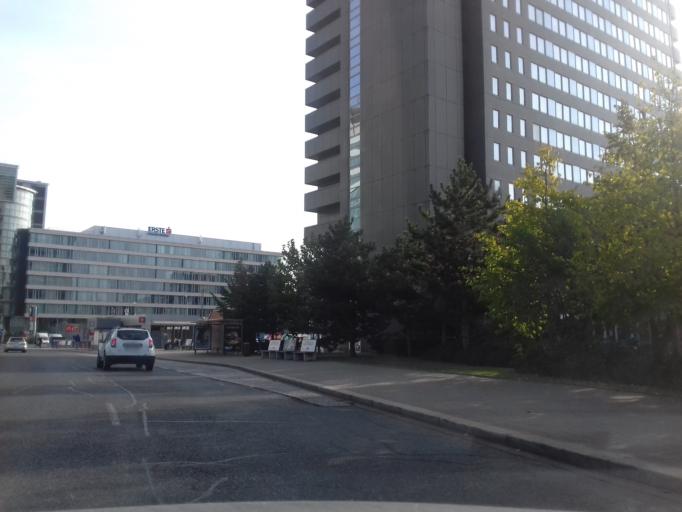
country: CZ
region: Praha
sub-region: Praha 4
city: Hodkovicky
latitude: 50.0442
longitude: 14.4471
